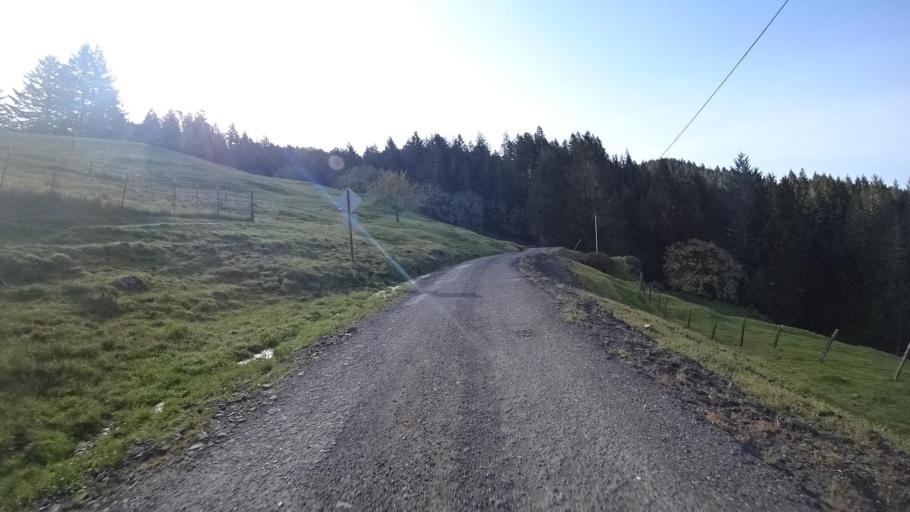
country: US
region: California
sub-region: Humboldt County
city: Bayside
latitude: 40.6872
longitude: -123.9378
